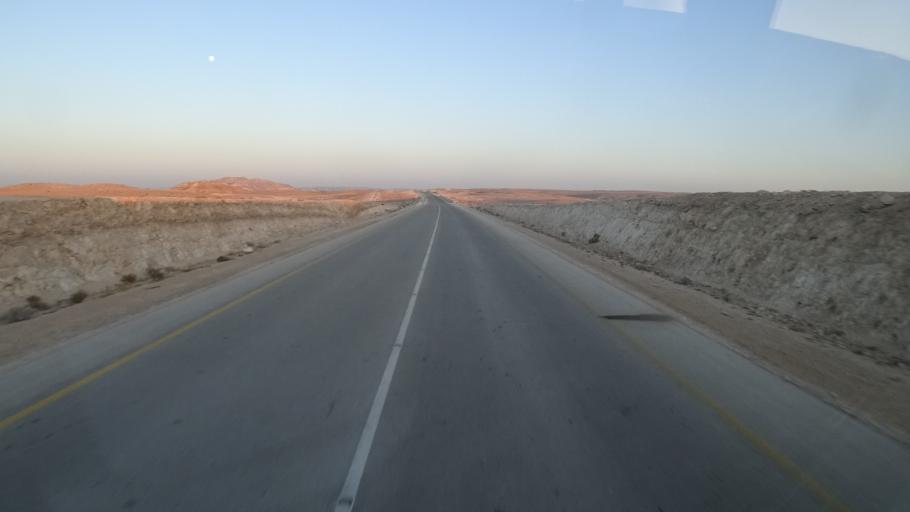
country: YE
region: Al Mahrah
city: Hawf
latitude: 16.9504
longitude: 53.3504
